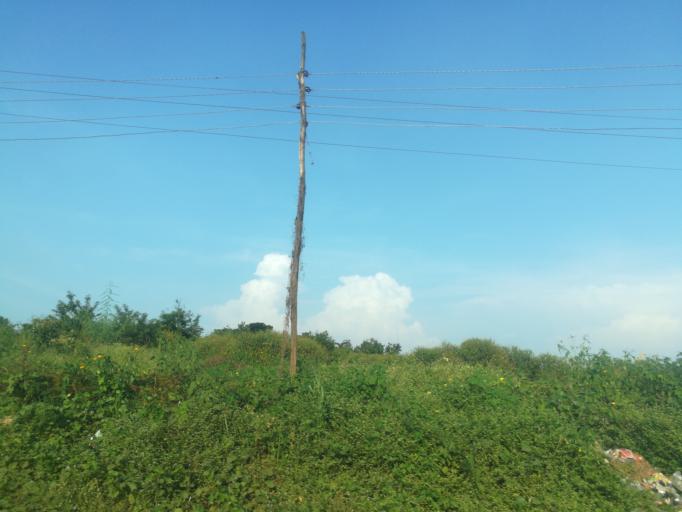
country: NG
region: Oyo
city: Moniya
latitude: 7.5517
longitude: 3.8908
